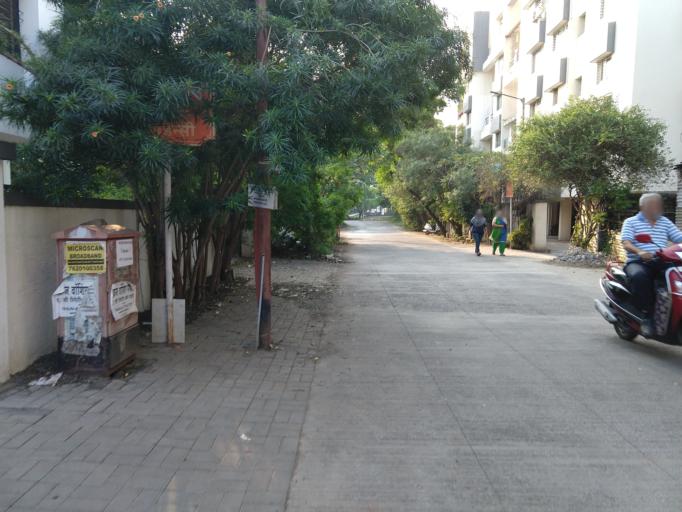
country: IN
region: Maharashtra
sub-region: Pune Division
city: Pune
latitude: 18.5091
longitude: 73.7931
